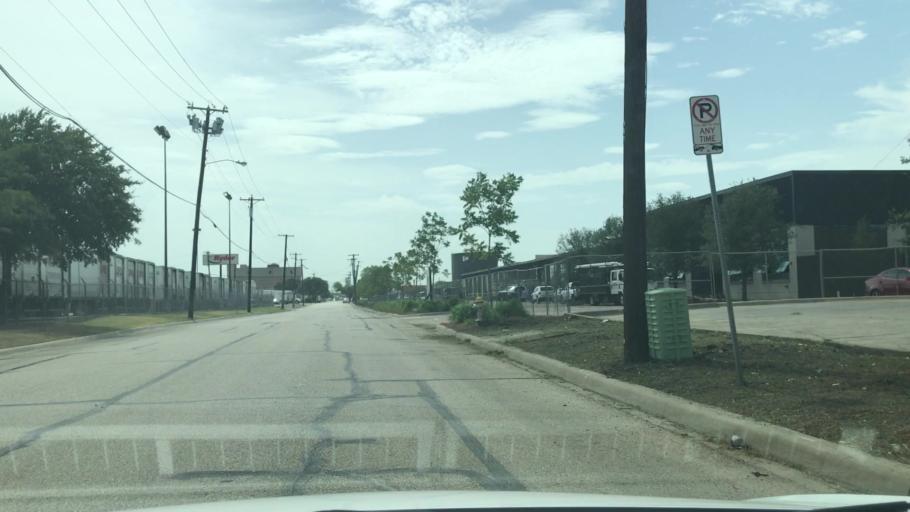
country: US
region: Texas
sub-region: Dallas County
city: Dallas
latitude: 32.8120
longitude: -96.8673
